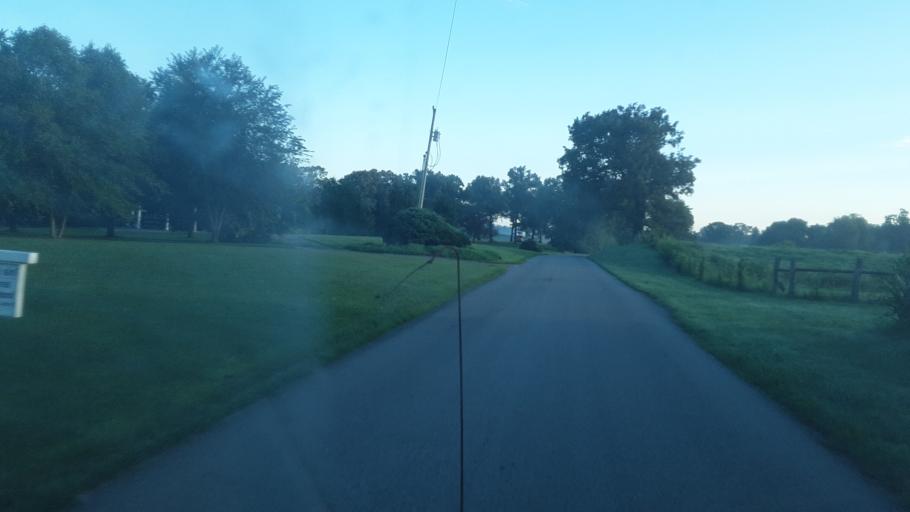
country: US
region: Kentucky
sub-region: Todd County
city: Elkton
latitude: 36.7355
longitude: -87.1677
